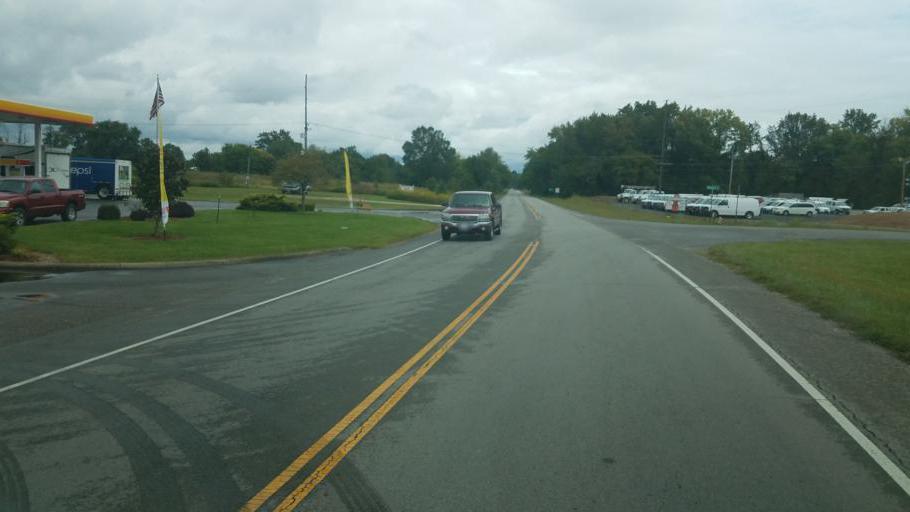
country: US
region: Ohio
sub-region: Scioto County
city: Wheelersburg
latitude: 38.6924
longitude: -82.8587
